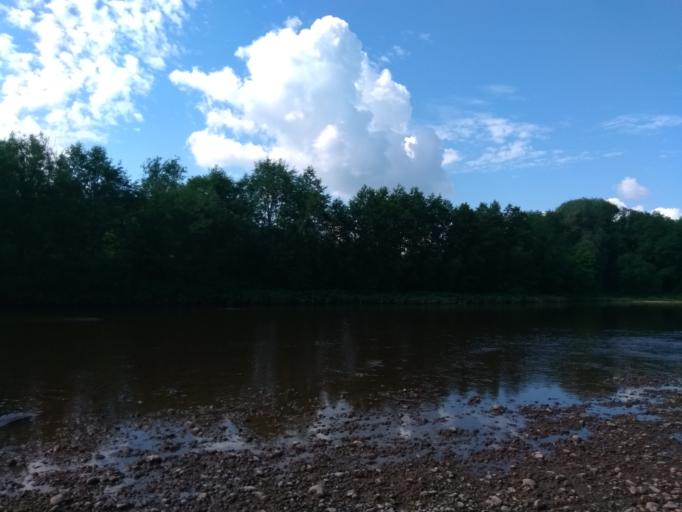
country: RU
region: Perm
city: Orda
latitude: 57.2113
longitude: 56.5882
